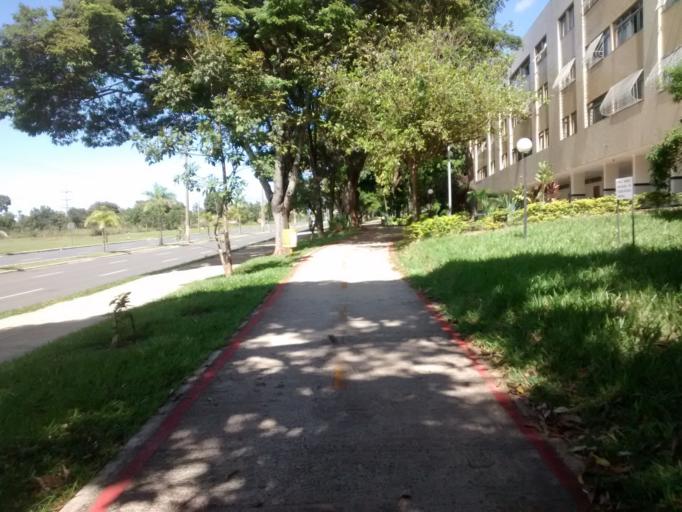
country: BR
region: Federal District
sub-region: Brasilia
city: Brasilia
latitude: -15.7358
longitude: -47.8859
